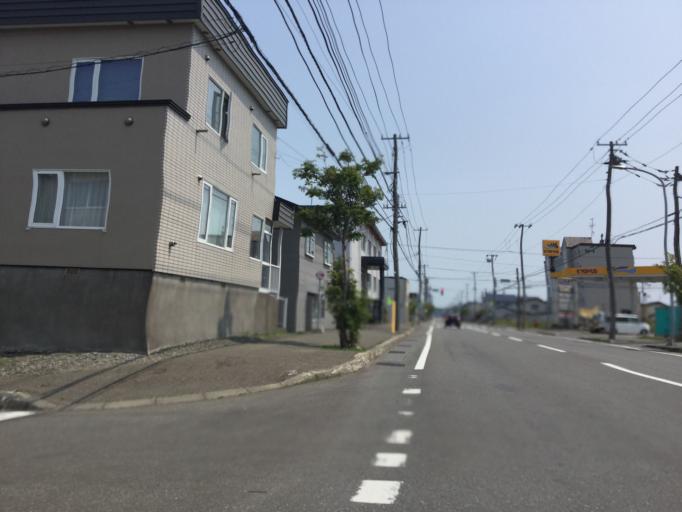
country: JP
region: Hokkaido
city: Wakkanai
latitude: 45.3950
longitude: 141.6977
